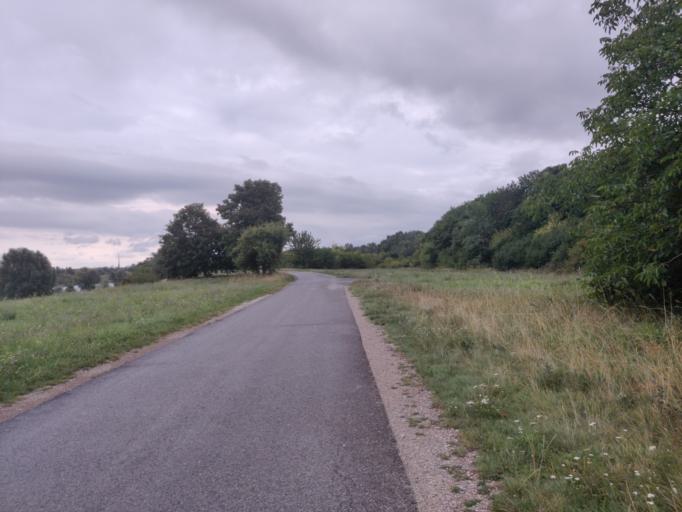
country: AT
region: Lower Austria
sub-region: Politischer Bezirk Korneuburg
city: Langenzersdorf
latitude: 48.2749
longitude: 16.3640
